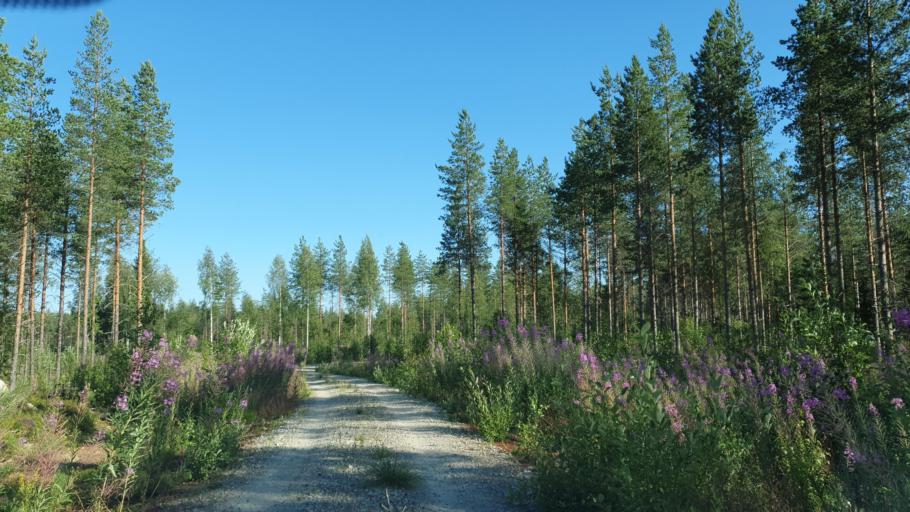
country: FI
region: Kainuu
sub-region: Kehys-Kainuu
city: Kuhmo
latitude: 64.0021
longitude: 29.7750
